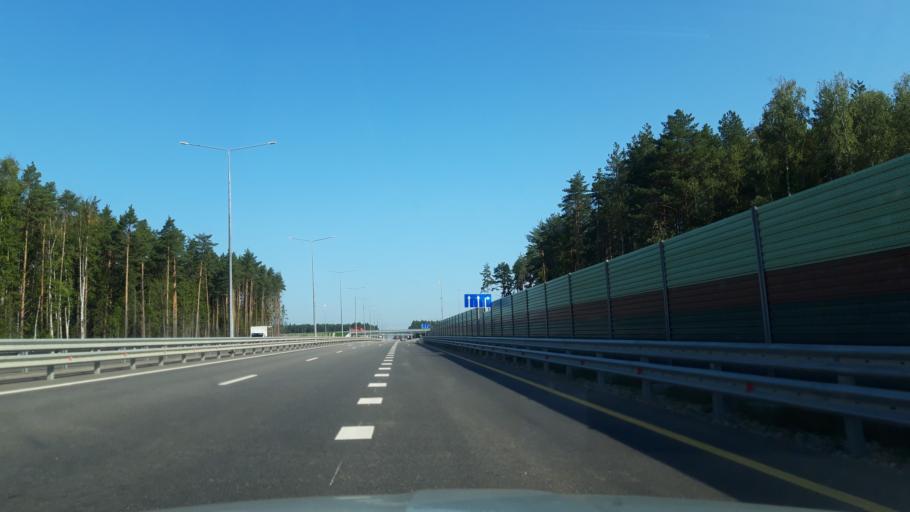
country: RU
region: Tverskaya
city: Novozavidovskiy
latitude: 56.5662
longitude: 36.4805
